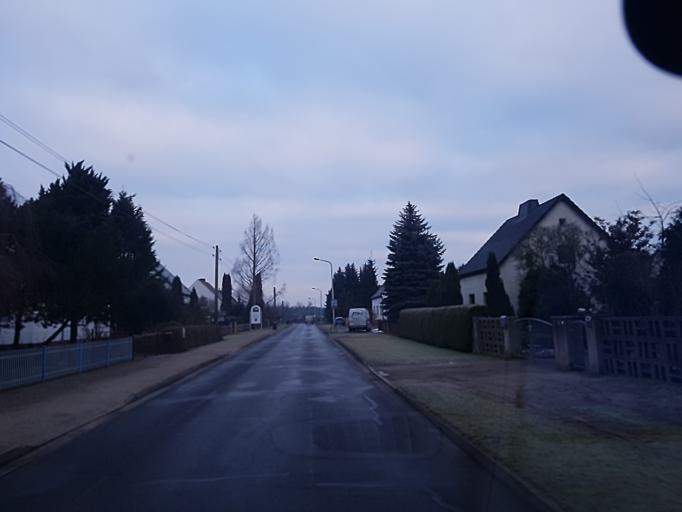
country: DE
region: Brandenburg
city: Finsterwalde
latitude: 51.6440
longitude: 13.7098
